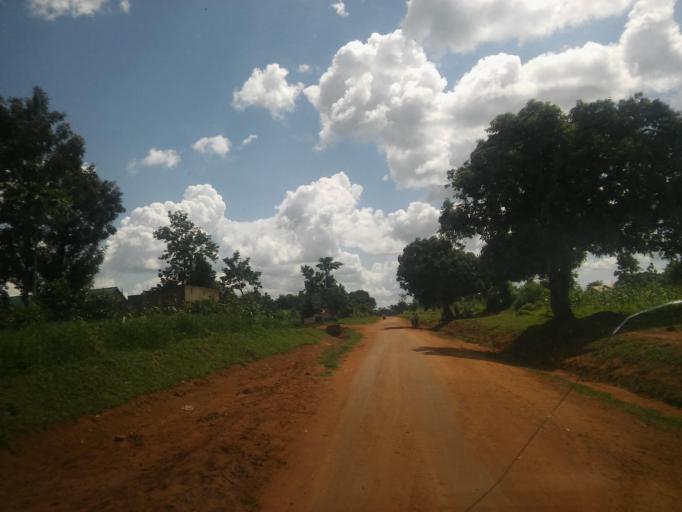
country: UG
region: Eastern Region
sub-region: Pallisa District
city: Pallisa
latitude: 1.1510
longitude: 33.8114
